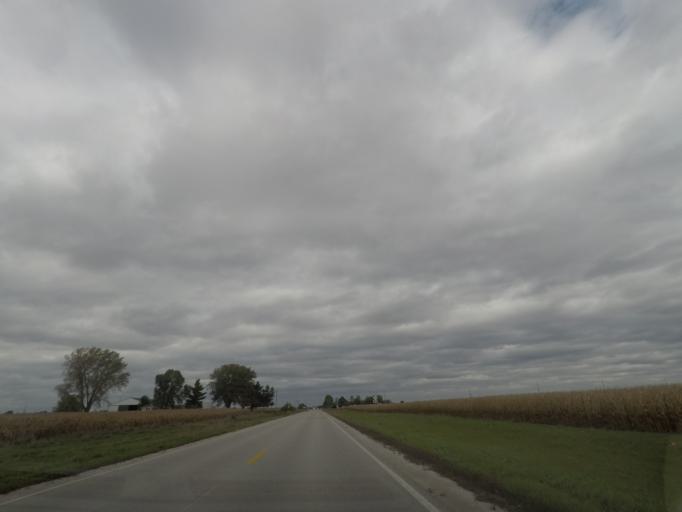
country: US
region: Iowa
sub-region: Story County
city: Huxley
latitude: 41.8746
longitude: -93.5314
